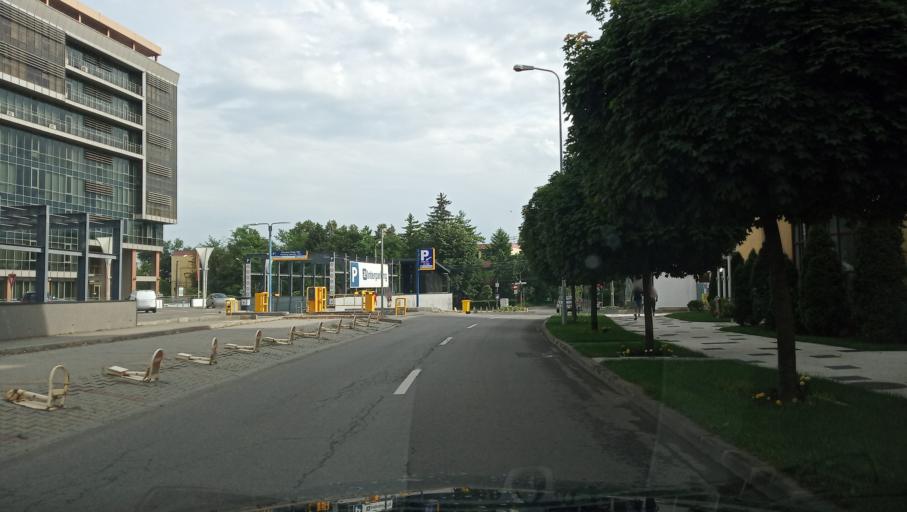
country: RO
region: Timis
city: Timisoara
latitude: 45.7577
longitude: 21.2223
